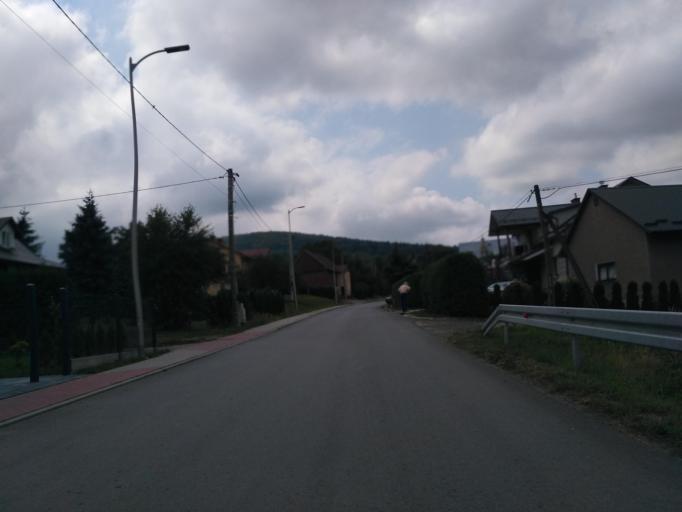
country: PL
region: Subcarpathian Voivodeship
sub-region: Powiat krosnienski
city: Iwonicz-Zdroj
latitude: 49.5726
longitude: 21.8190
